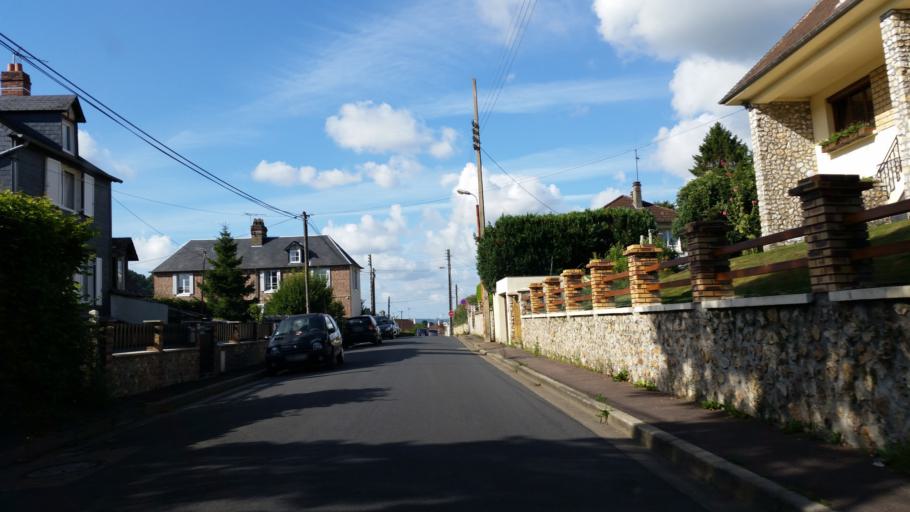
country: FR
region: Lower Normandy
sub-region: Departement du Calvados
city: Honfleur
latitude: 49.4091
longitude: 0.2276
